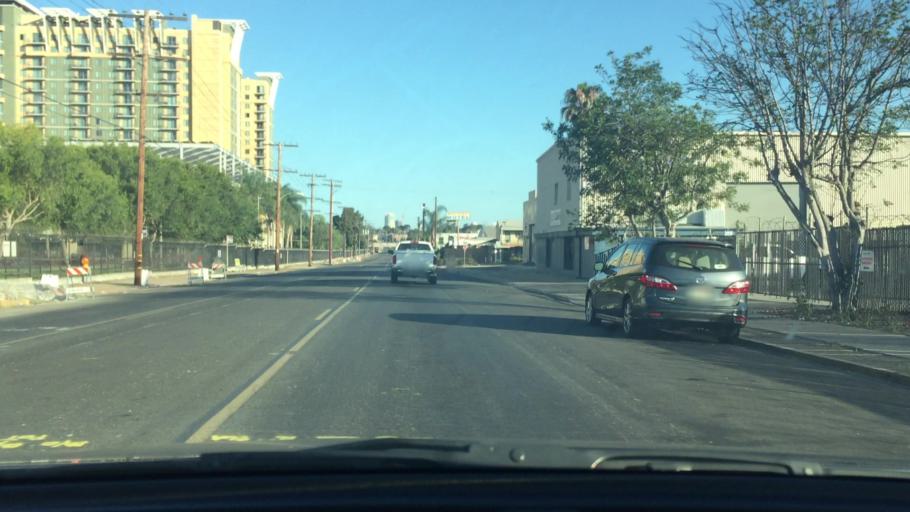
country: US
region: California
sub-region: San Diego County
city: National City
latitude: 32.6871
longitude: -117.1178
